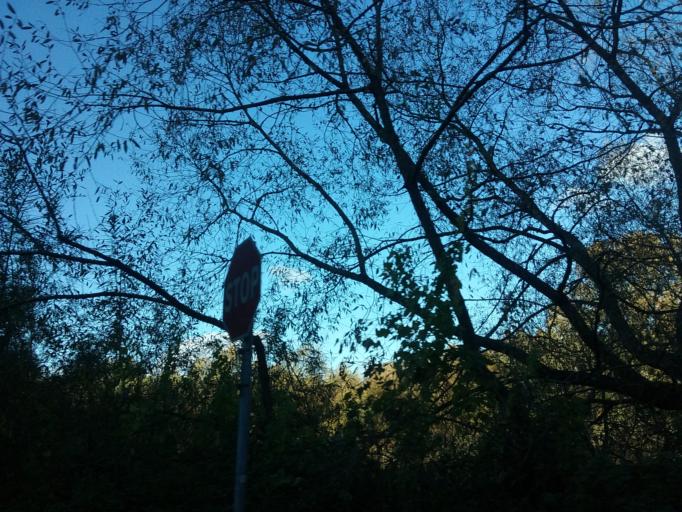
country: IE
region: Leinster
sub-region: Lu
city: Tullyallen
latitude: 53.7180
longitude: -6.3997
